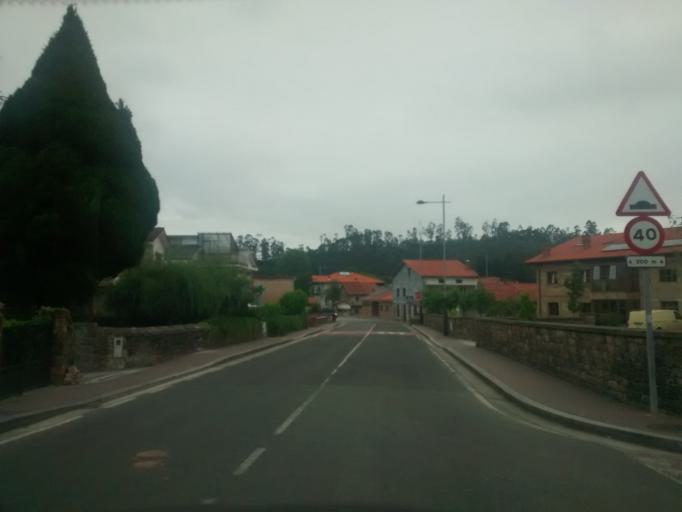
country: ES
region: Cantabria
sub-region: Provincia de Cantabria
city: Luzmela
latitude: 43.3166
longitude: -4.1921
